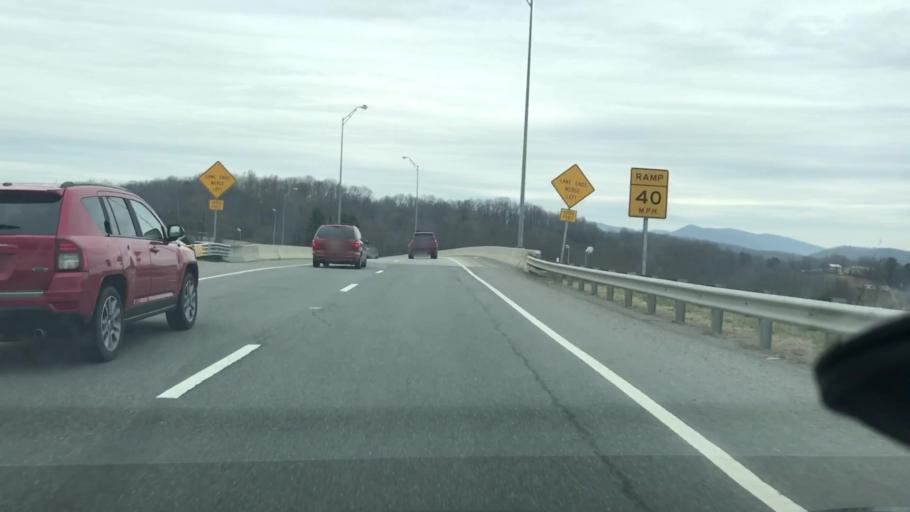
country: US
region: Virginia
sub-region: Montgomery County
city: Christiansburg
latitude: 37.1550
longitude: -80.4128
